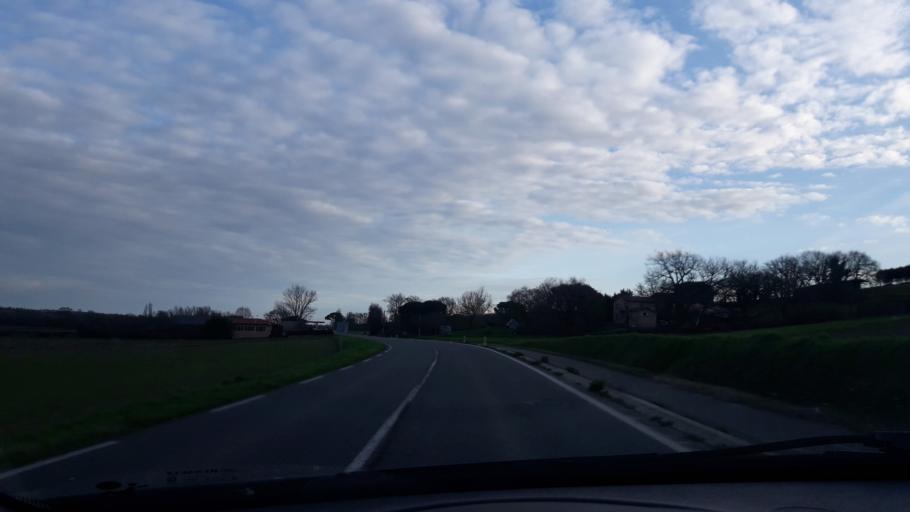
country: FR
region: Midi-Pyrenees
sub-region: Departement de la Haute-Garonne
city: Levignac
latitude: 43.6726
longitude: 1.2028
